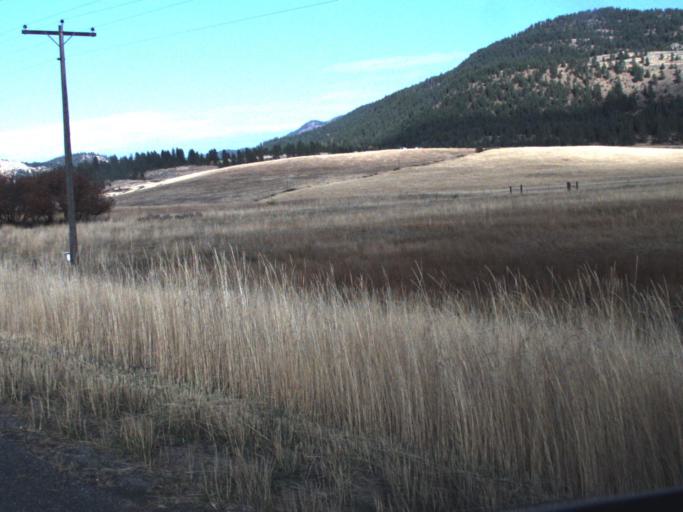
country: US
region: Washington
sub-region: Stevens County
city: Kettle Falls
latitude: 48.4341
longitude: -118.1709
